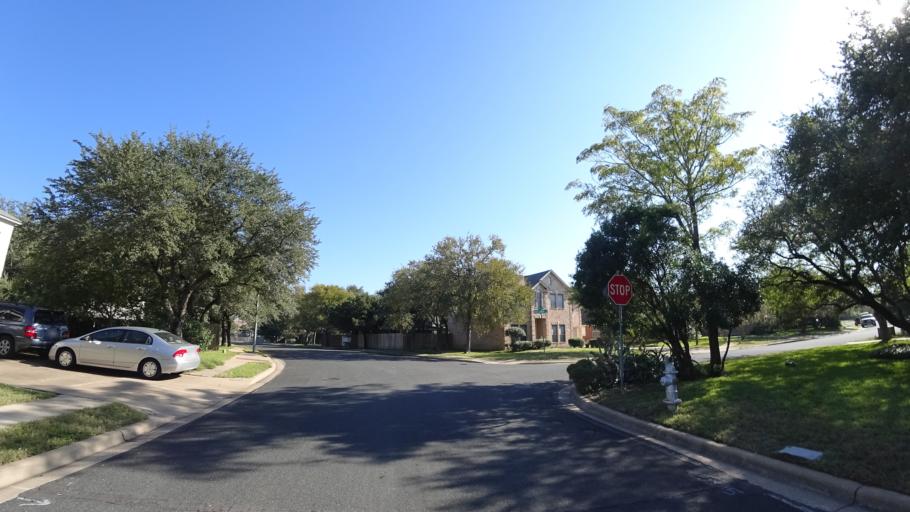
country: US
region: Texas
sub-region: Travis County
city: Shady Hollow
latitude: 30.2069
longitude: -97.8575
